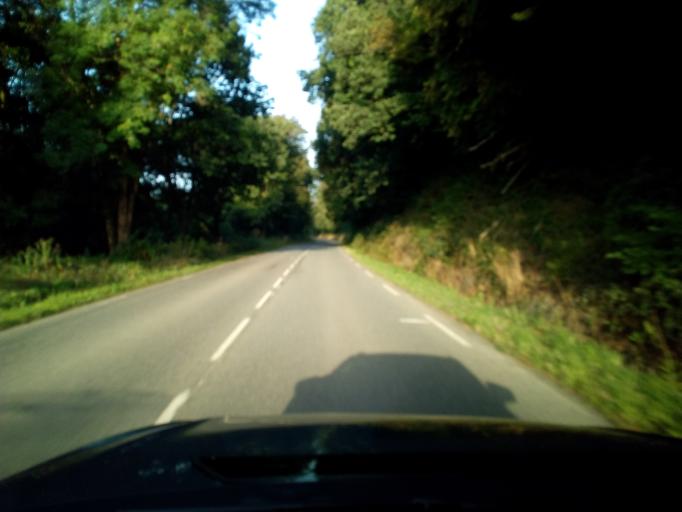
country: FR
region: Brittany
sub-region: Departement du Finistere
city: La Roche-Maurice
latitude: 48.4882
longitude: -4.1642
